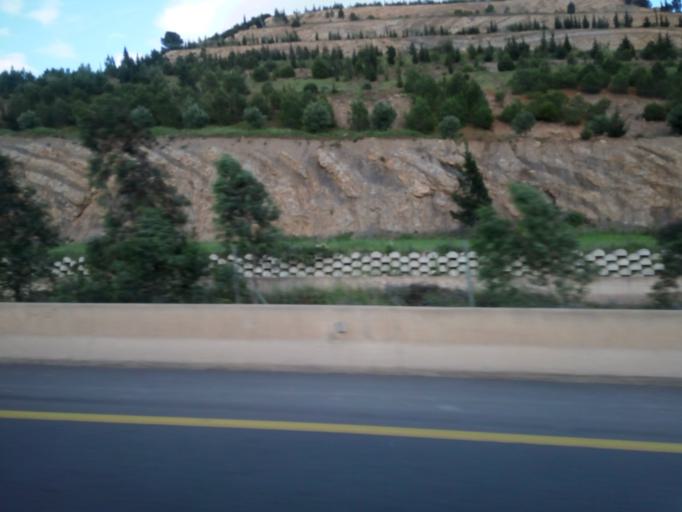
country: DZ
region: Tipaza
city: El Affroun
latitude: 36.4146
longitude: 2.5618
